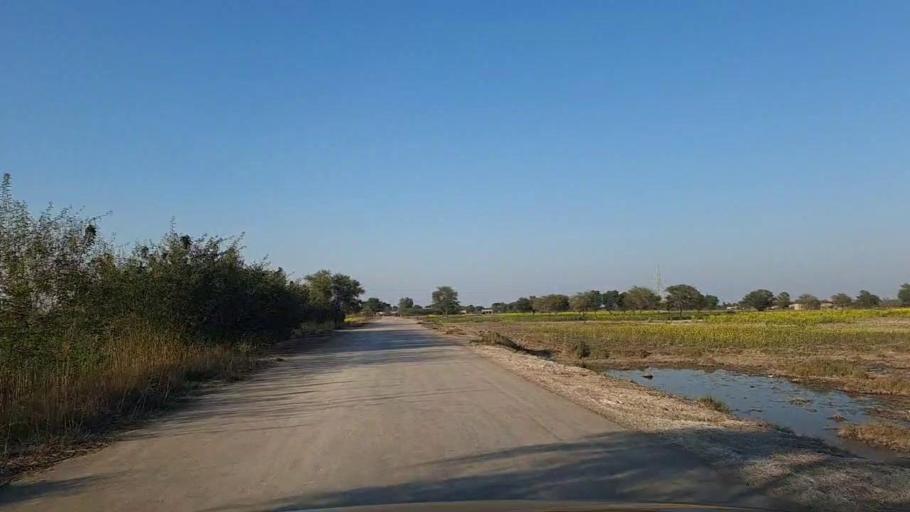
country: PK
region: Sindh
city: Nawabshah
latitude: 26.2224
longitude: 68.3432
